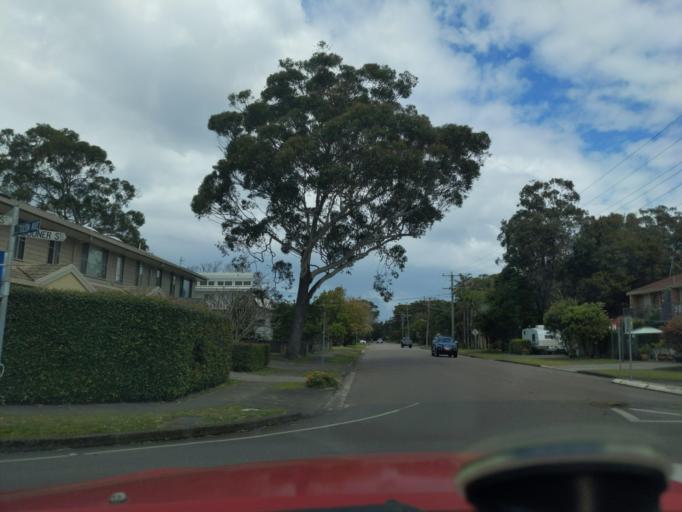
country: AU
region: New South Wales
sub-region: Great Lakes
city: Hawks Nest
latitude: -32.6727
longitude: 152.1774
